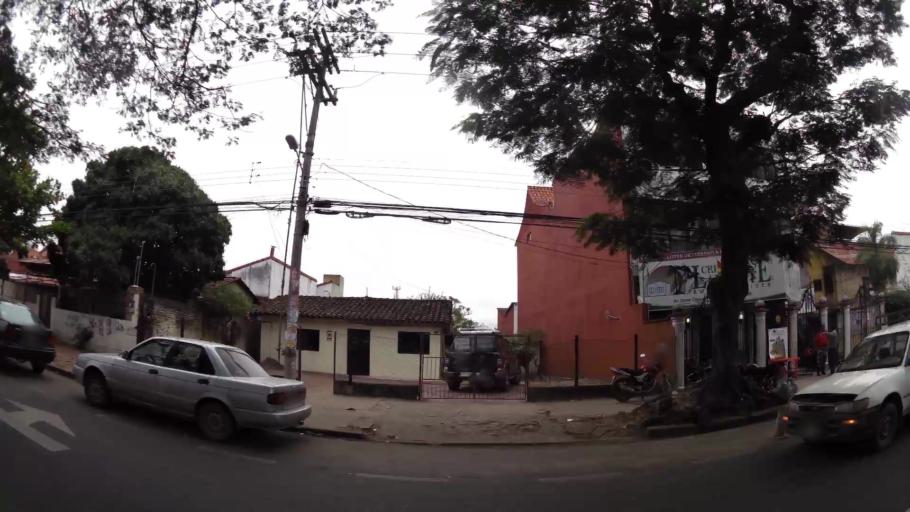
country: BO
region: Santa Cruz
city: Santa Cruz de la Sierra
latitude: -17.7975
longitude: -63.1864
